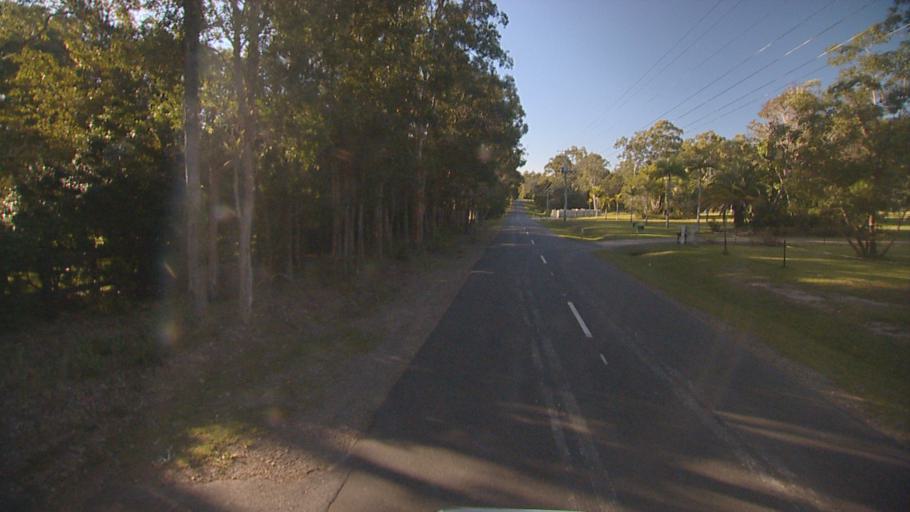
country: AU
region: Queensland
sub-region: Redland
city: Redland Bay
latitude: -27.6776
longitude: 153.2757
